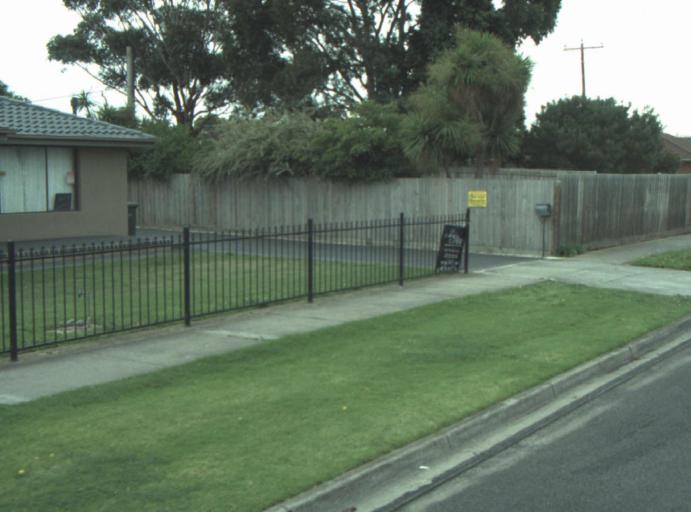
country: AU
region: Victoria
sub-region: Greater Geelong
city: Breakwater
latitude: -38.1767
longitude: 144.3903
